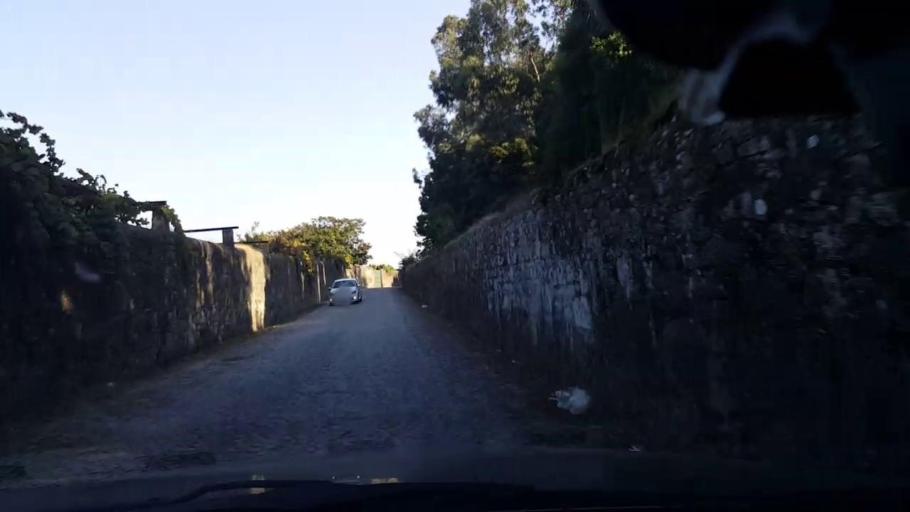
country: PT
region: Porto
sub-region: Vila do Conde
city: Arvore
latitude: 41.3410
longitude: -8.6858
